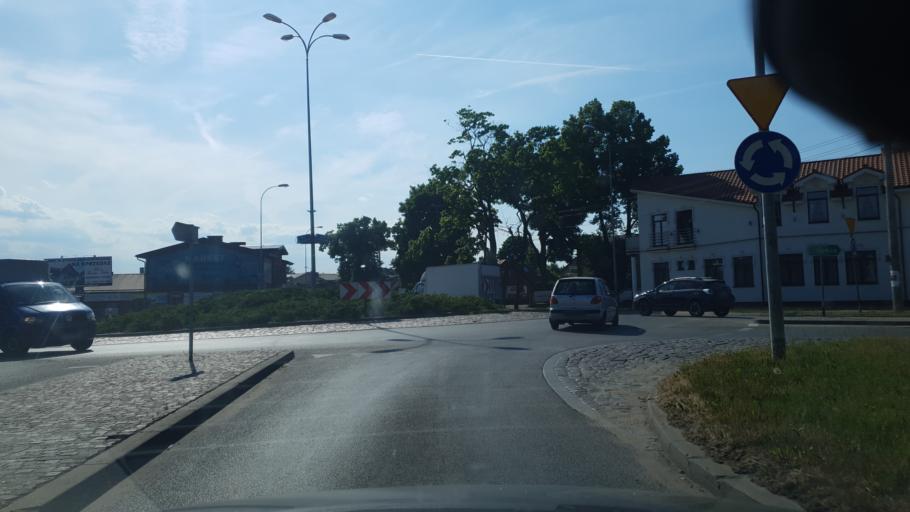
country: PL
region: Pomeranian Voivodeship
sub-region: Powiat kartuski
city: Chwaszczyno
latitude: 54.4436
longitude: 18.4194
